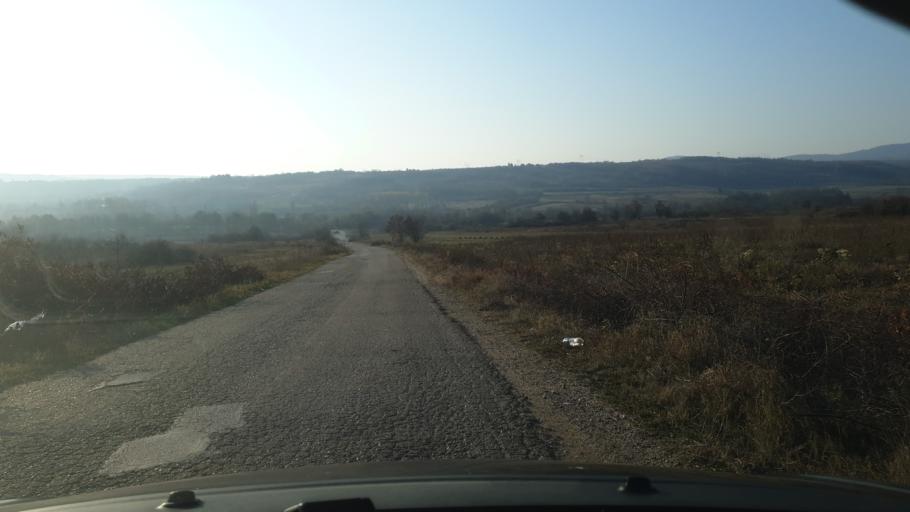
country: RS
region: Central Serbia
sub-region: Borski Okrug
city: Negotin
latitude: 44.1218
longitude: 22.3344
